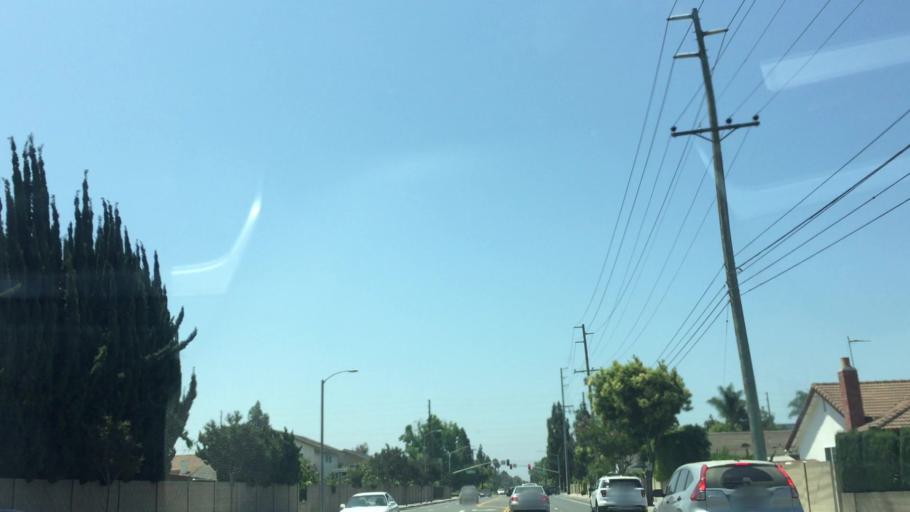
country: US
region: California
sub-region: Orange County
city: Fountain Valley
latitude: 33.7184
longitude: -117.9285
